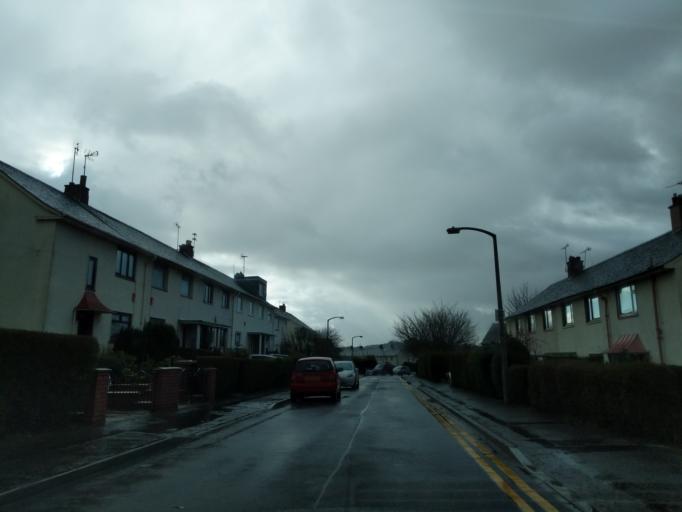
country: GB
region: Scotland
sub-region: Midlothian
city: Loanhead
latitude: 55.9204
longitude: -3.1494
